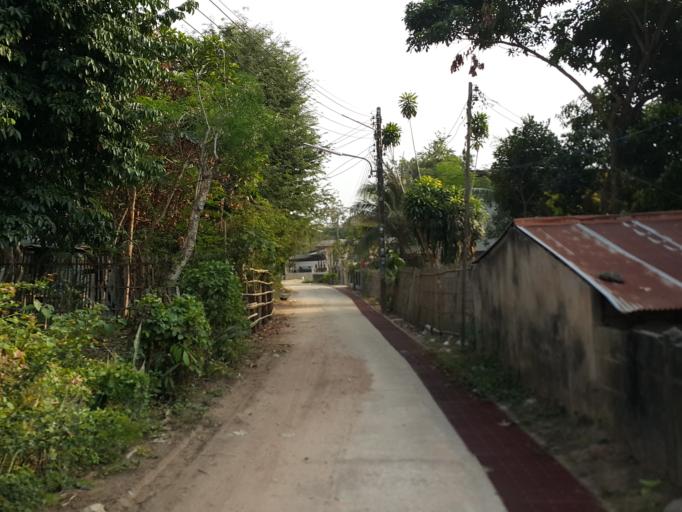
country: TH
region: Chiang Mai
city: San Sai
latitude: 18.8709
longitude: 99.1383
